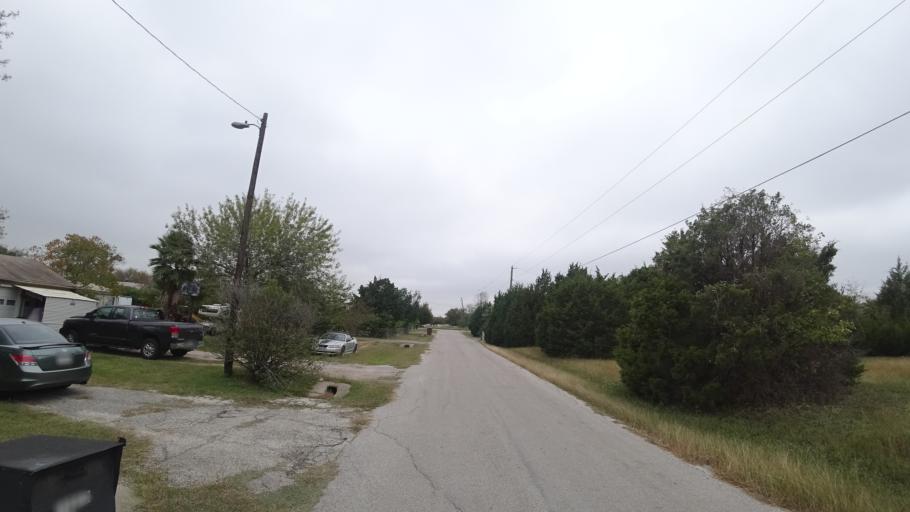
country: US
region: Texas
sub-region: Travis County
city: Pflugerville
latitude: 30.3727
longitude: -97.6213
